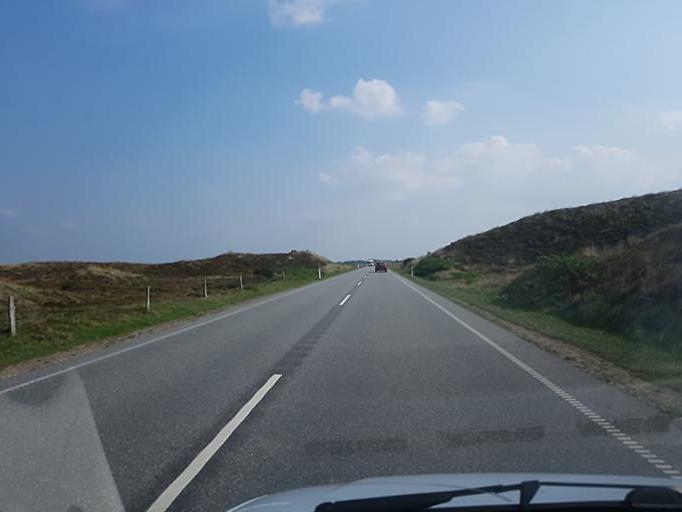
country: DK
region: Central Jutland
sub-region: Ringkobing-Skjern Kommune
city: Hvide Sande
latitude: 55.8963
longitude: 8.1697
